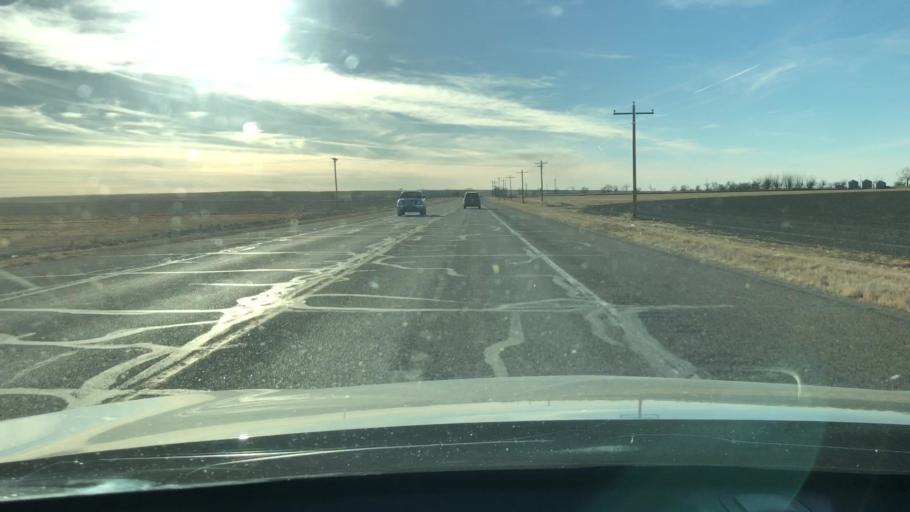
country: US
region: Colorado
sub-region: Prowers County
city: Lamar
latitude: 38.0639
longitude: -102.3413
